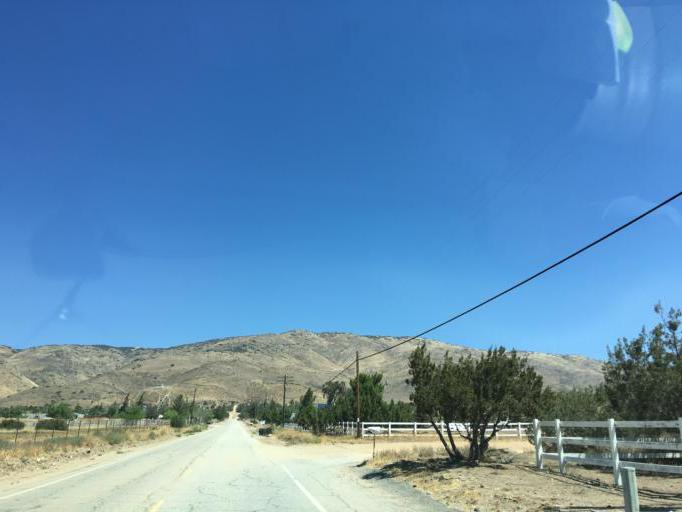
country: US
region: California
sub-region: Los Angeles County
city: Acton
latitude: 34.5192
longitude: -118.2380
